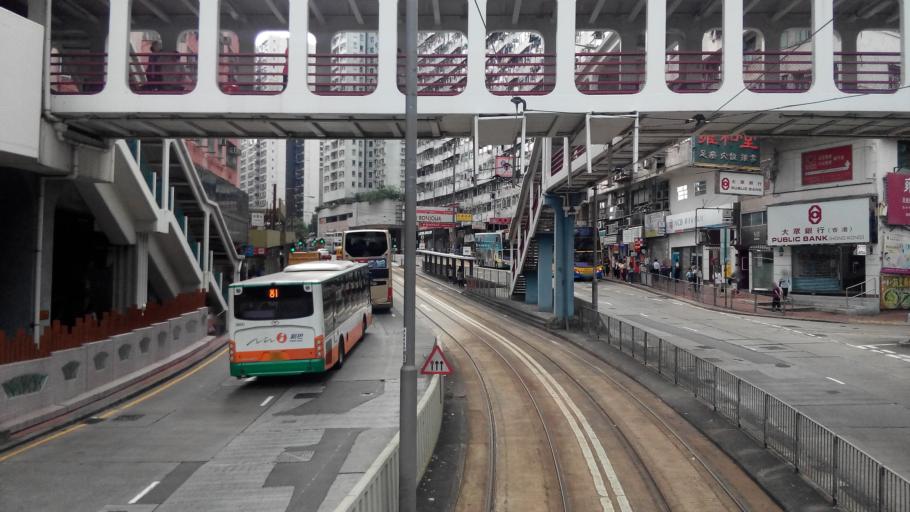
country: HK
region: Wanchai
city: Wan Chai
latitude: 22.2851
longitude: 114.2116
